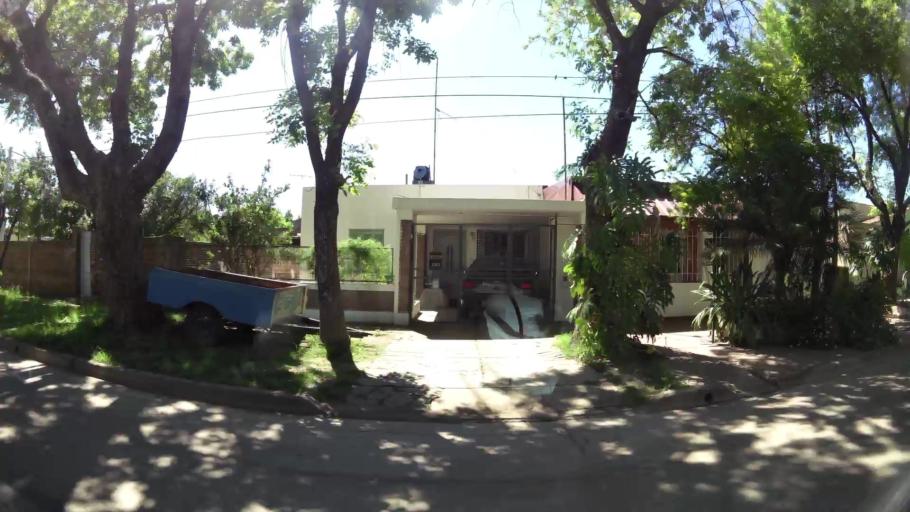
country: AR
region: Santa Fe
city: Esperanza
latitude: -31.4375
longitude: -60.9297
